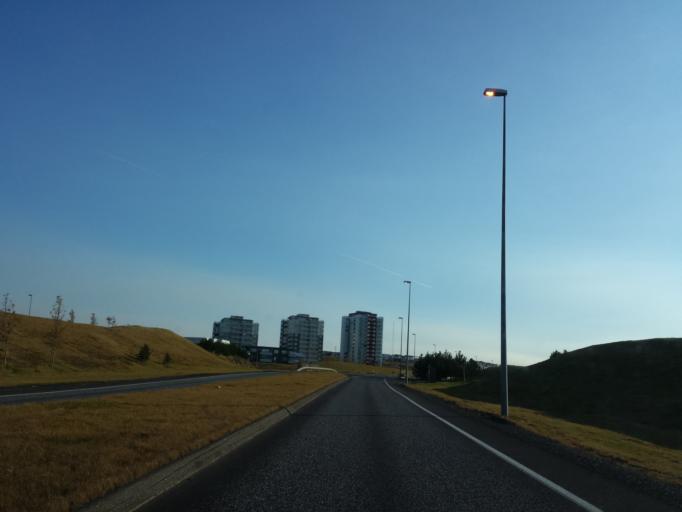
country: IS
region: Capital Region
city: Reykjavik
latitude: 64.0893
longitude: -21.8479
